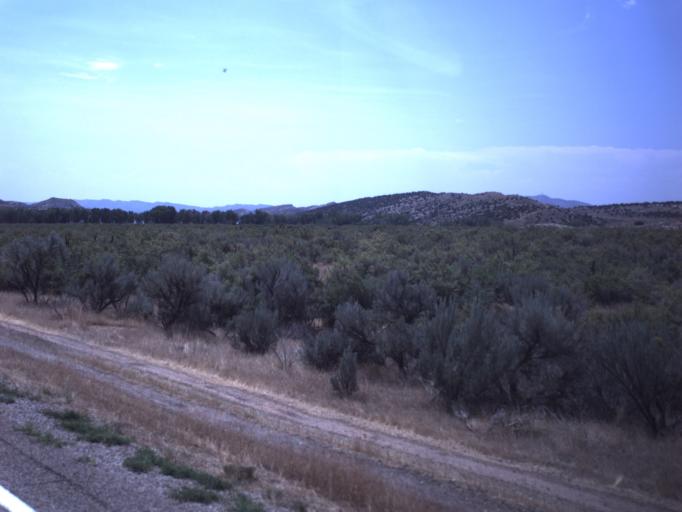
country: US
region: Utah
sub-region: Uintah County
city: Vernal
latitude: 40.5405
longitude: -109.5246
